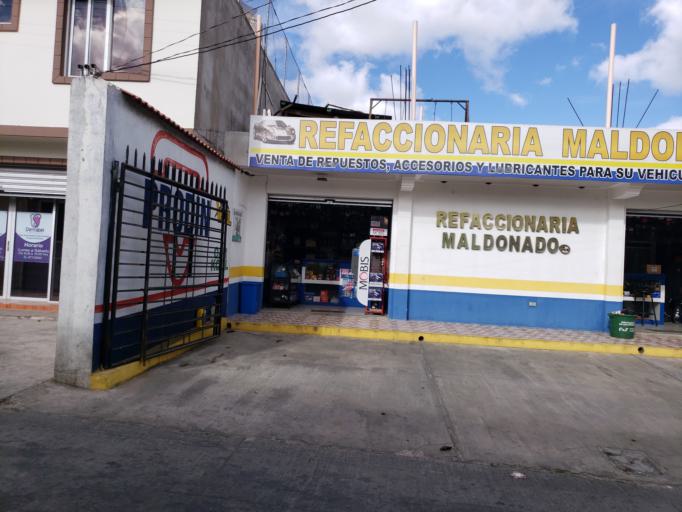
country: GT
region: Quetzaltenango
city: Ostuncalco
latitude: 14.8661
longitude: -91.6219
